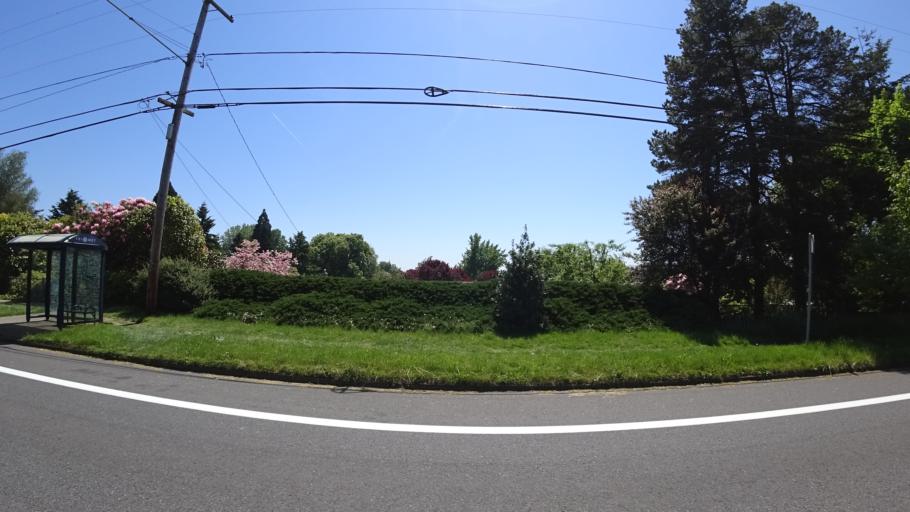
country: US
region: Oregon
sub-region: Multnomah County
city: Portland
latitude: 45.4761
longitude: -122.6909
